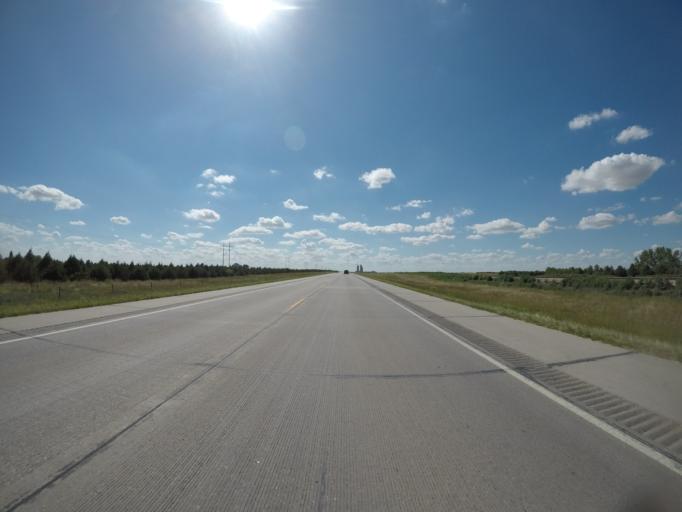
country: US
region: Colorado
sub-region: Phillips County
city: Holyoke
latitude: 40.5874
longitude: -102.3238
